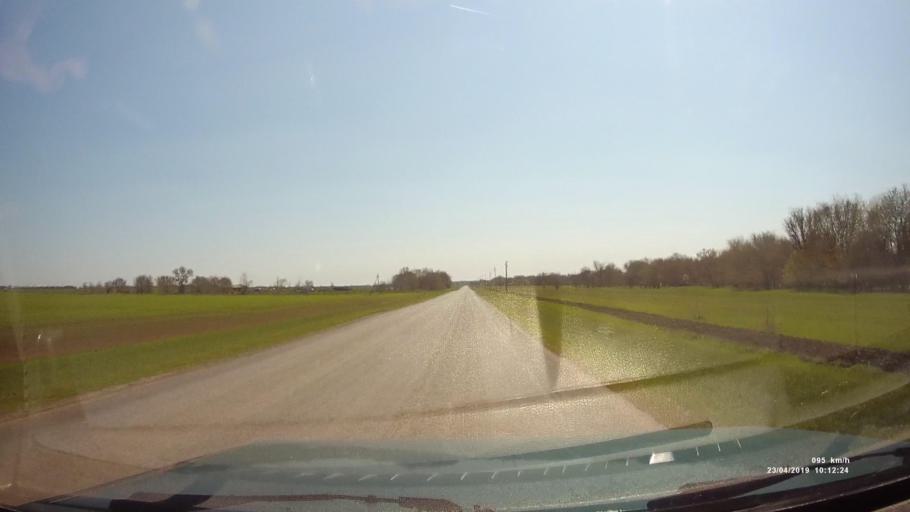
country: RU
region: Rostov
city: Sovetskoye
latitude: 46.6903
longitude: 42.3349
